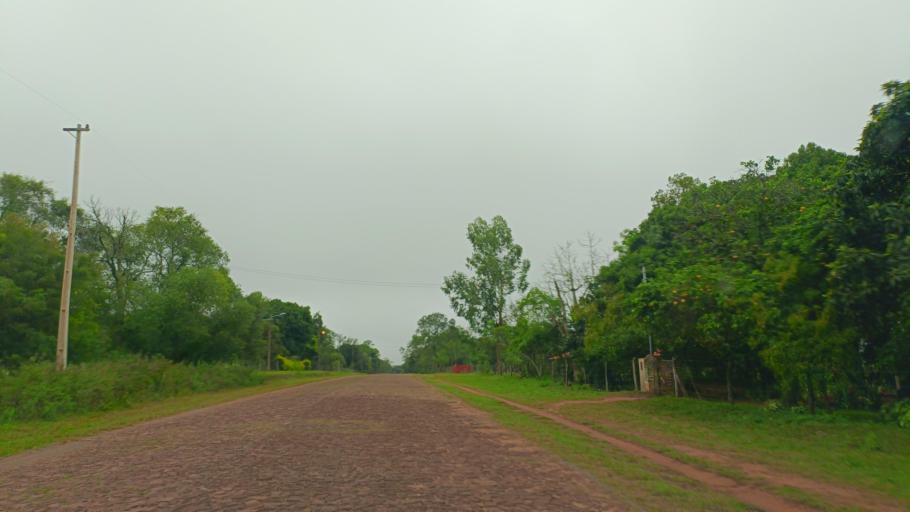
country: PY
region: Misiones
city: Santa Maria
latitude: -26.8709
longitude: -57.0117
